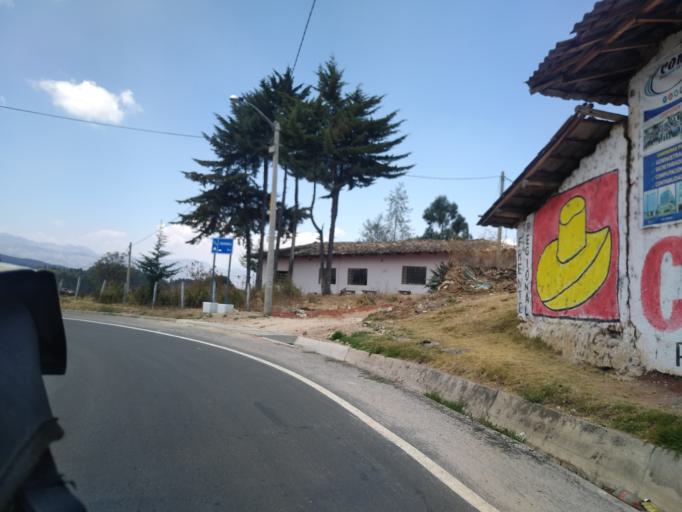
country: PE
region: Cajamarca
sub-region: San Marcos
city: San Marcos
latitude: -7.2807
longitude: -78.2397
